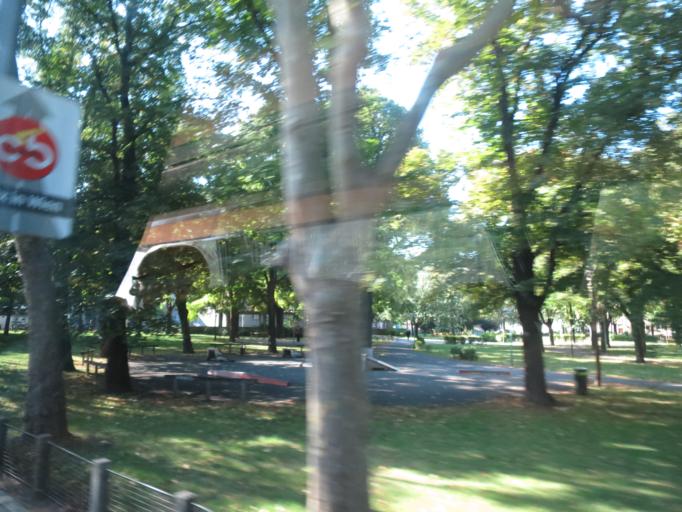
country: AT
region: Vienna
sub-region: Wien Stadt
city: Vienna
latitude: 48.1820
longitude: 16.3471
